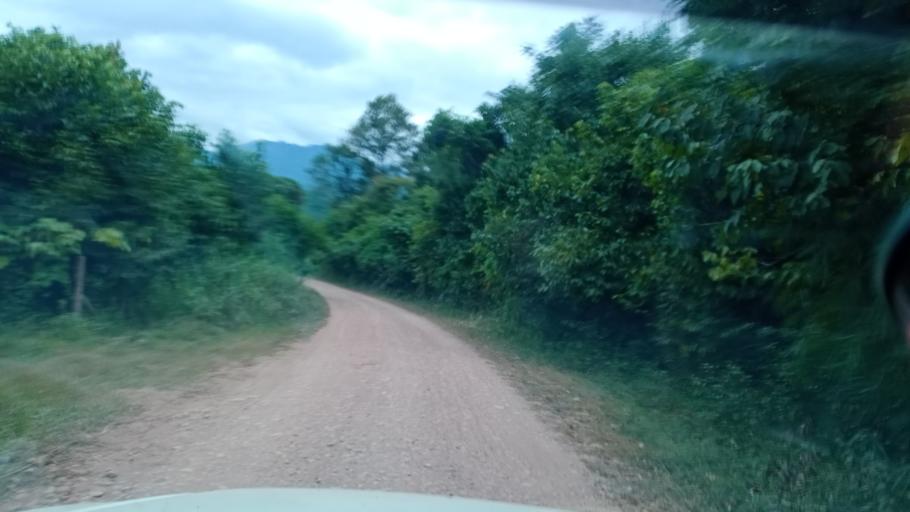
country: TH
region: Changwat Bueng Kan
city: Pak Khat
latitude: 18.7155
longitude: 103.2224
